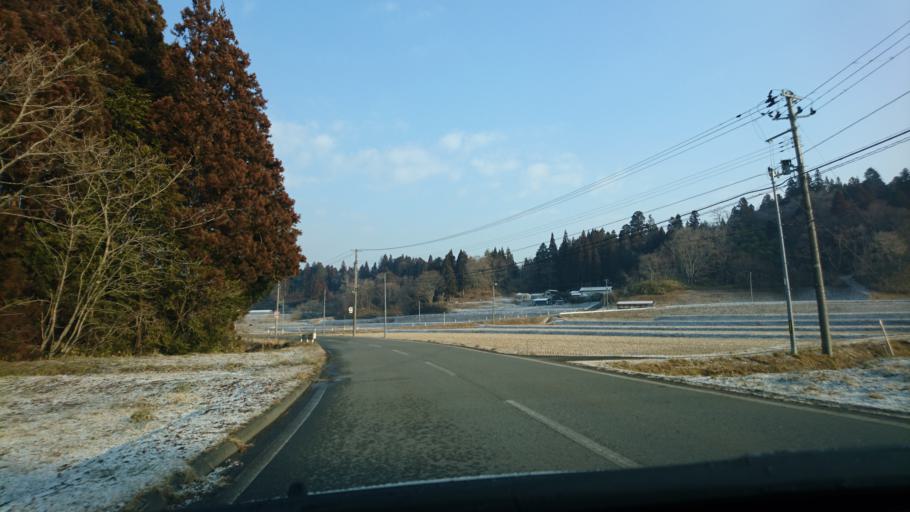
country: JP
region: Iwate
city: Ichinoseki
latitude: 38.9270
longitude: 141.3864
